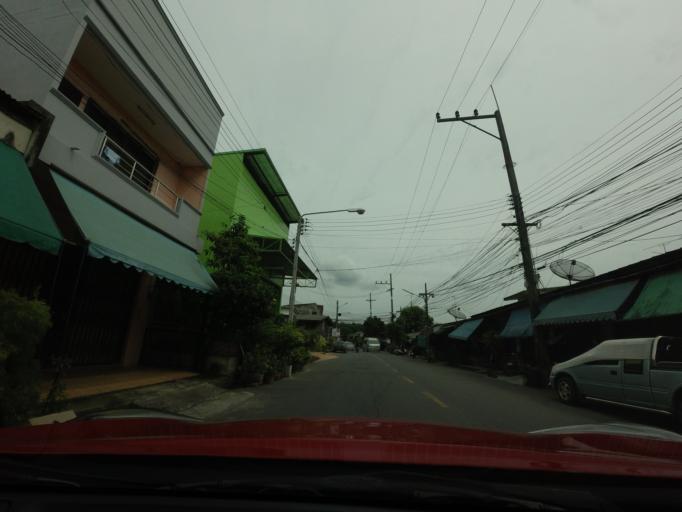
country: TH
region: Songkhla
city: Hat Yai
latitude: 6.9919
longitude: 100.4771
